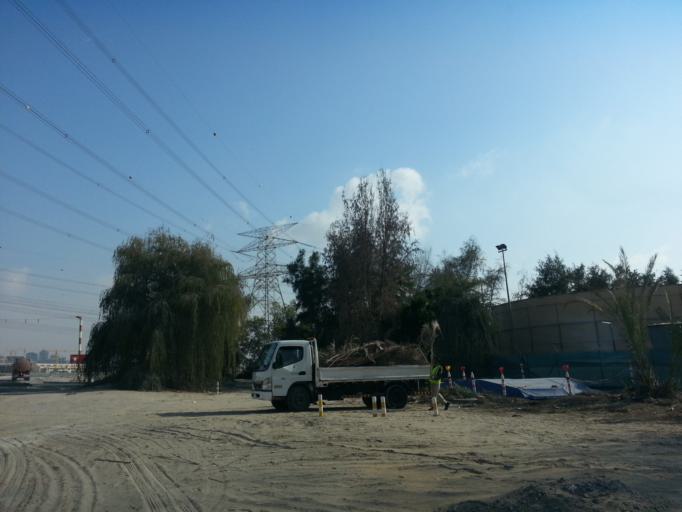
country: AE
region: Dubai
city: Dubai
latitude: 25.0651
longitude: 55.1939
